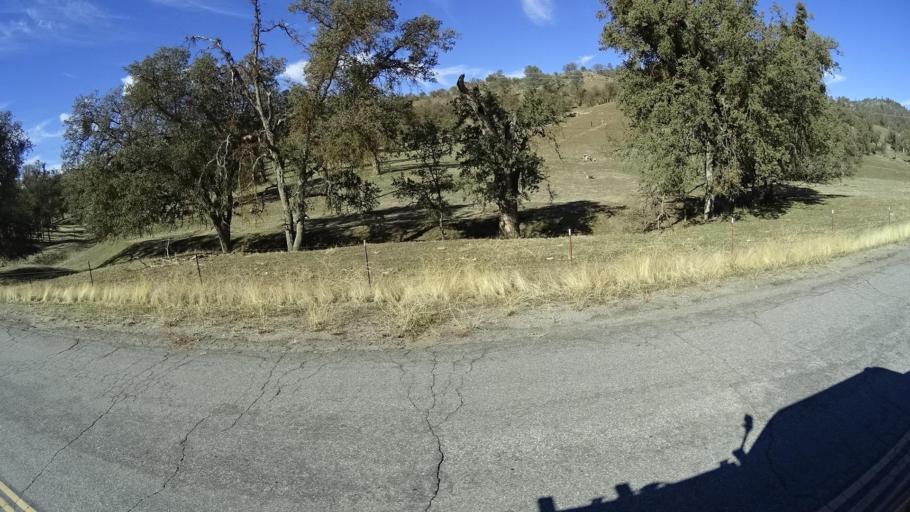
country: US
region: California
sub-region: Kern County
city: Alta Sierra
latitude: 35.6315
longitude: -118.7651
